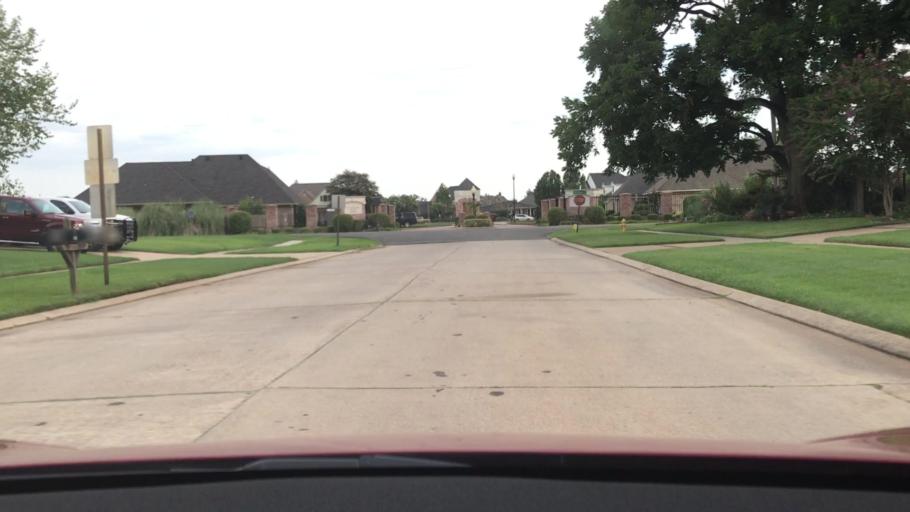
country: US
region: Louisiana
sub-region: Bossier Parish
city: Bossier City
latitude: 32.4537
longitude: -93.6704
